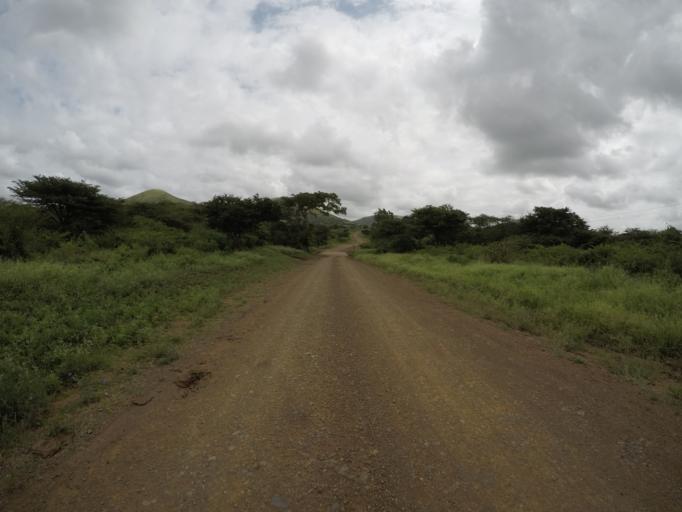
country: ZA
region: KwaZulu-Natal
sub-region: uThungulu District Municipality
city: Empangeni
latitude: -28.5966
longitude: 31.8917
